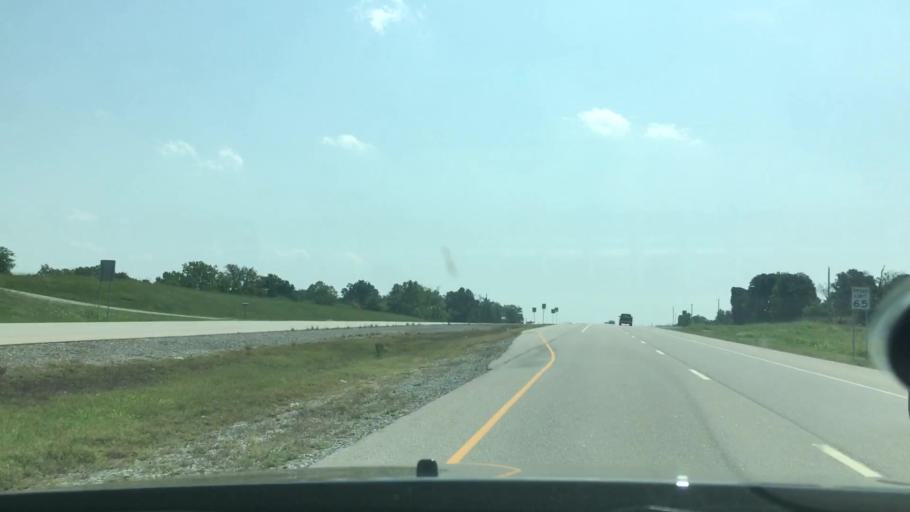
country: US
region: Oklahoma
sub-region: Atoka County
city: Atoka
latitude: 34.3506
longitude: -96.0831
